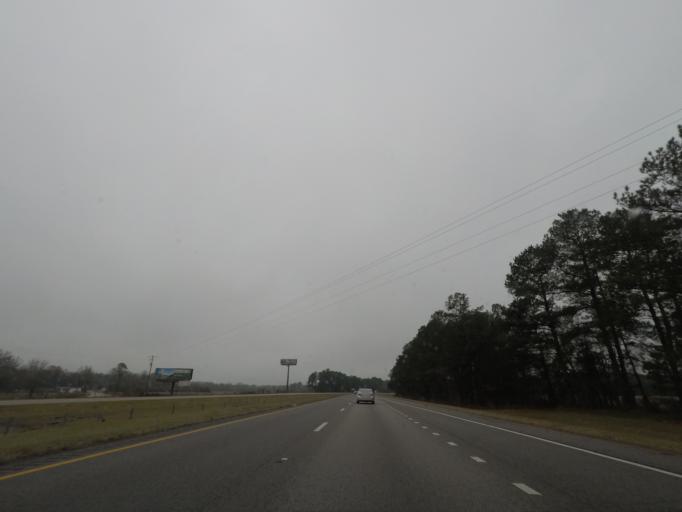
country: US
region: South Carolina
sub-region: Florence County
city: Timmonsville
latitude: 33.9640
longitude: -80.0442
